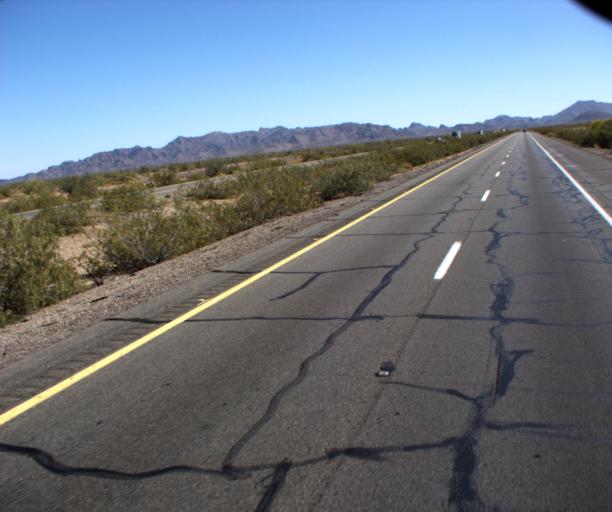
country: US
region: Arizona
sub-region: La Paz County
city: Quartzsite
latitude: 33.6706
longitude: -114.1560
